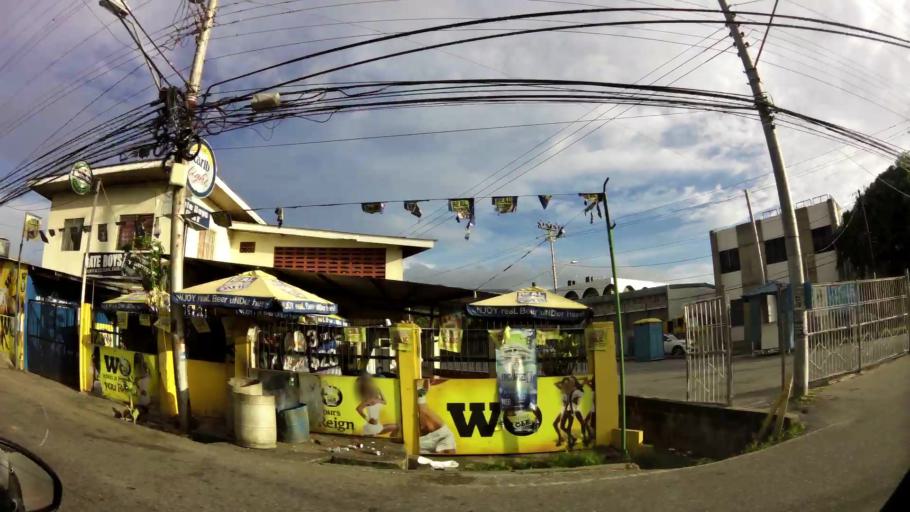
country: TT
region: Tunapuna/Piarco
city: Tunapuna
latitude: 10.6381
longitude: -61.4006
